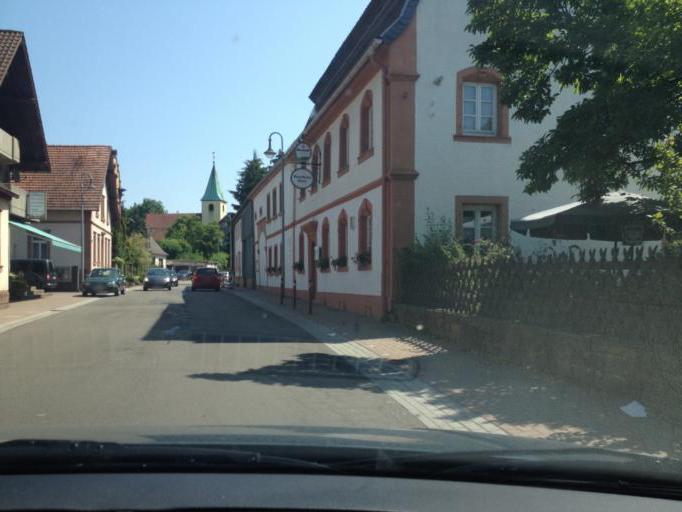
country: DE
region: Rheinland-Pfalz
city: Hutschenhausen
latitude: 49.4188
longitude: 7.4747
